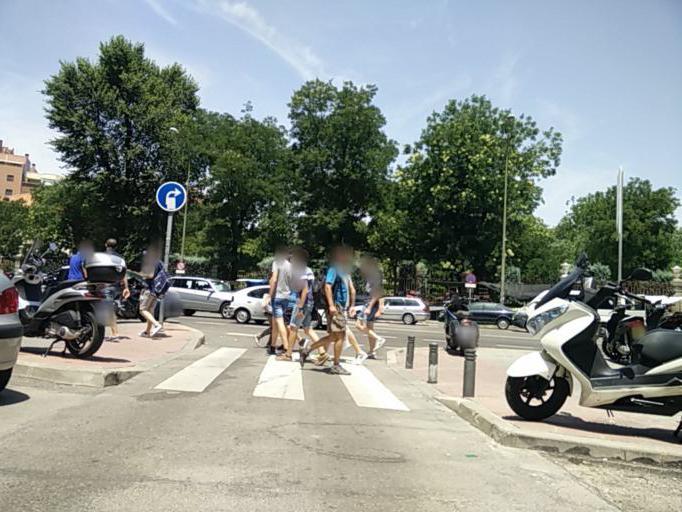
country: ES
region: Madrid
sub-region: Provincia de Madrid
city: Arganzuela
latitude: 40.4054
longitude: -3.7057
